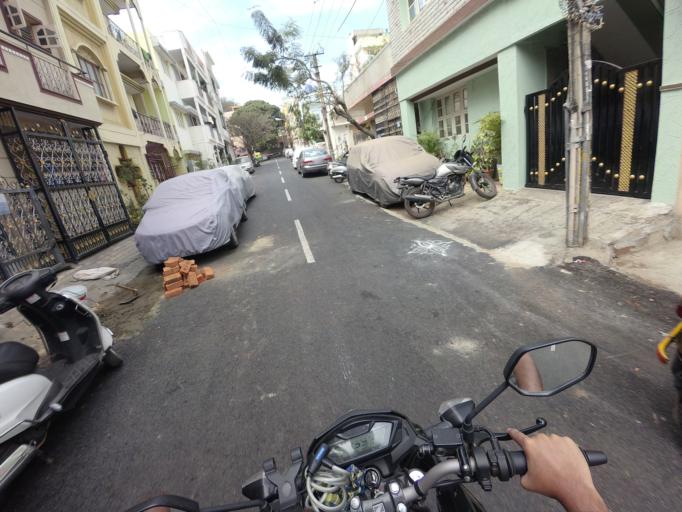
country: IN
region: Karnataka
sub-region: Bangalore Urban
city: Bangalore
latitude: 12.9693
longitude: 77.5453
